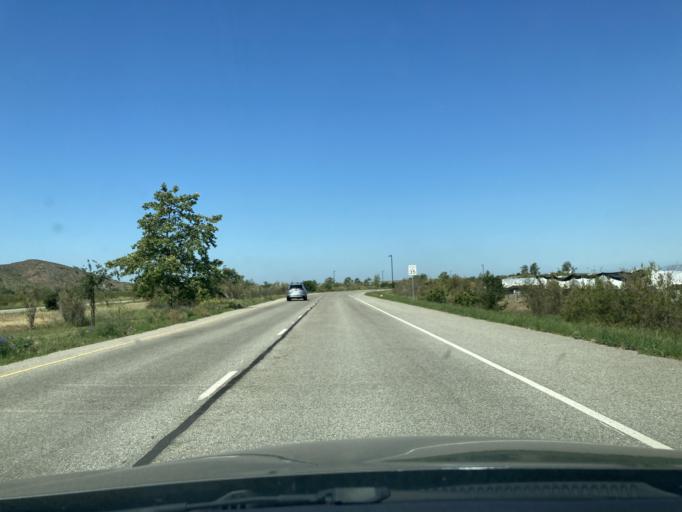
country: US
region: California
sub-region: Ventura County
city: Camarillo
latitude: 34.1686
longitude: -119.0484
